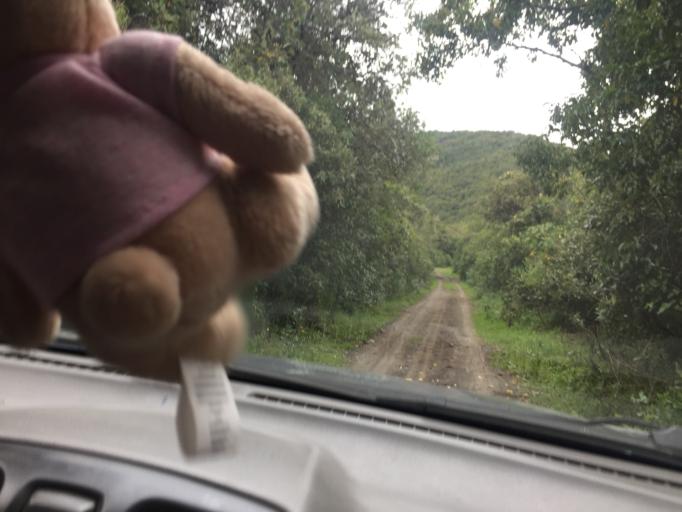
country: EC
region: Pichincha
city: Cayambe
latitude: 0.0768
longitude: -78.2991
